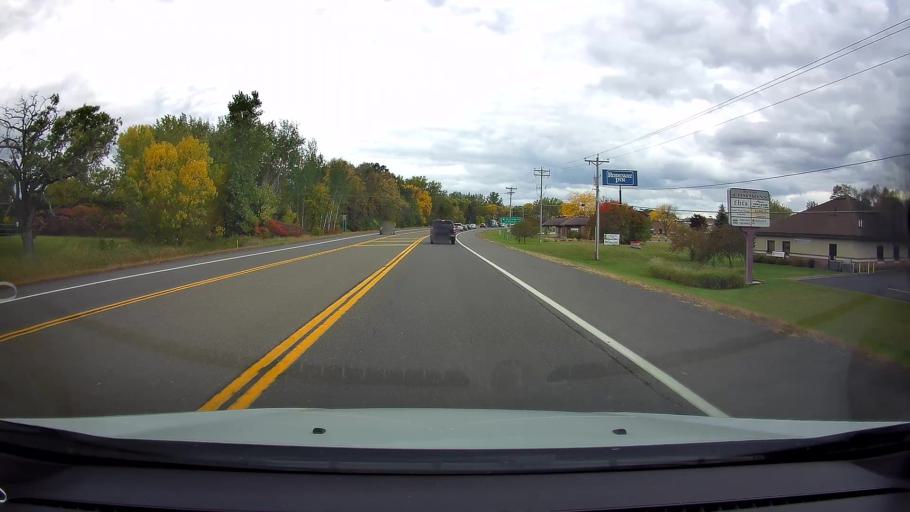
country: US
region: Minnesota
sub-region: Chisago County
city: Chisago City
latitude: 45.3822
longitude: -92.8701
